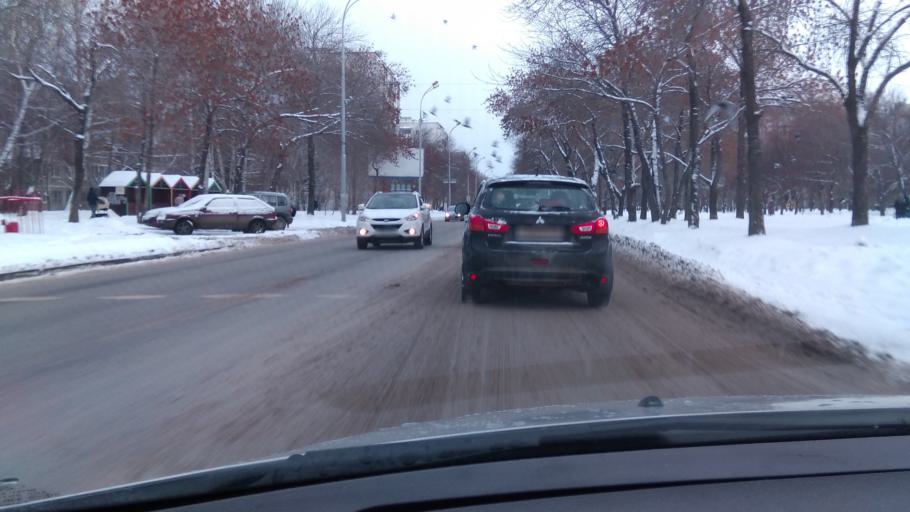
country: RU
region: Sverdlovsk
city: Sovkhoznyy
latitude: 56.8168
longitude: 60.5641
